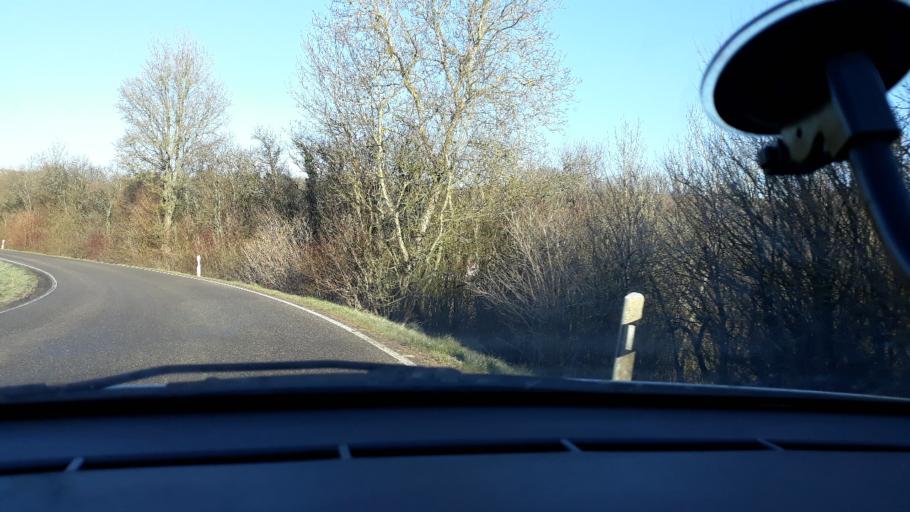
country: DE
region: Saarland
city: Blieskastel
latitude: 49.2119
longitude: 7.2315
